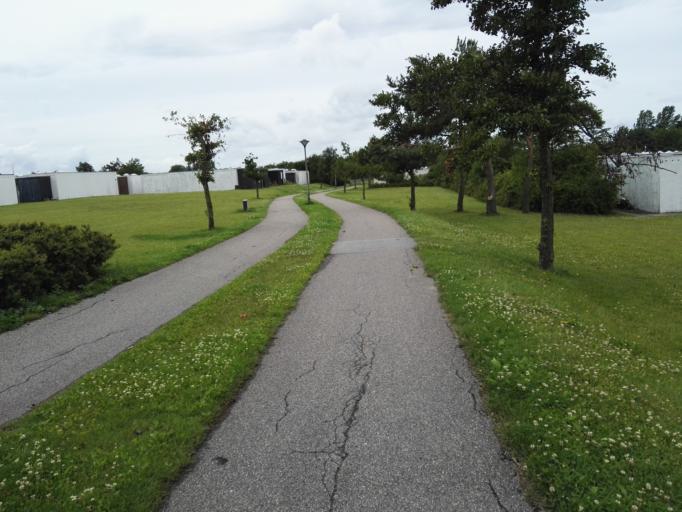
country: DK
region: Capital Region
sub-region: Egedal Kommune
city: Olstykke
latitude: 55.7771
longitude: 12.1640
